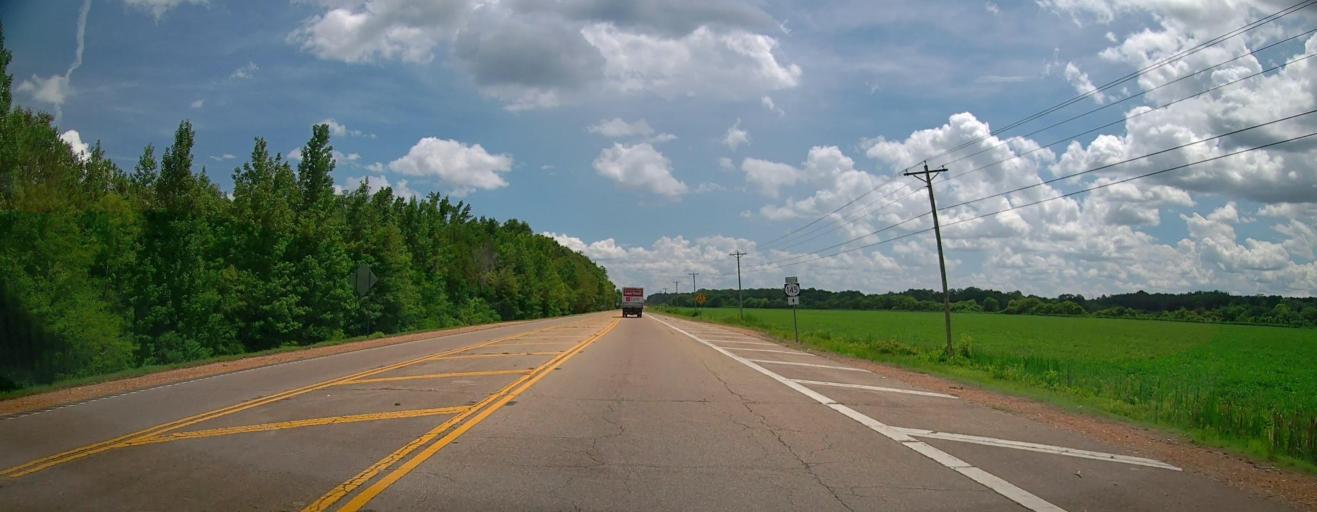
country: US
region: Mississippi
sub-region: Lee County
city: Shannon
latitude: 34.1499
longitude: -88.7195
